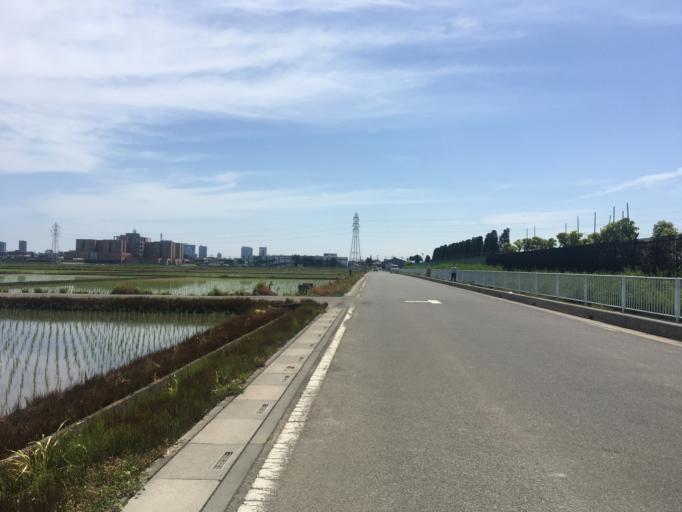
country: JP
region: Saitama
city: Yono
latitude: 35.8794
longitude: 139.5915
